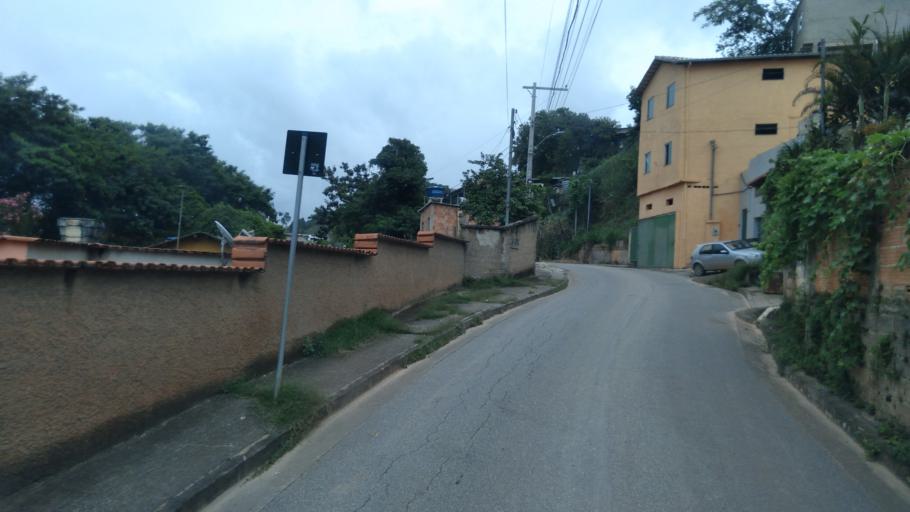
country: BR
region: Minas Gerais
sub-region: Santa Luzia
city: Santa Luzia
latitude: -19.8387
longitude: -43.8654
